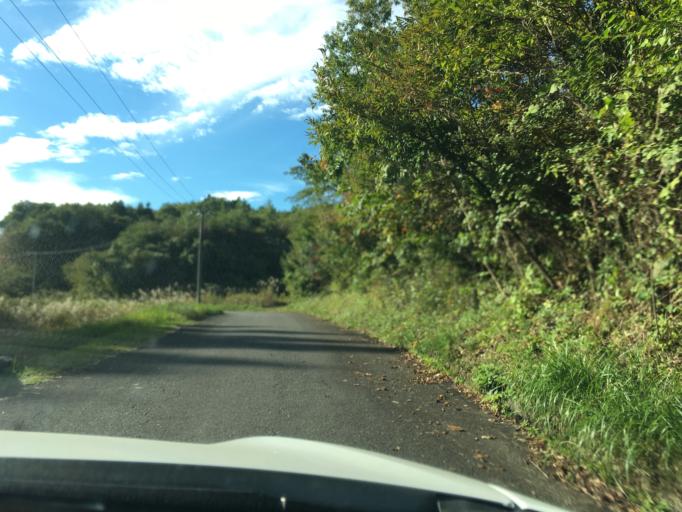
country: JP
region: Fukushima
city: Ishikawa
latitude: 37.1697
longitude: 140.4925
